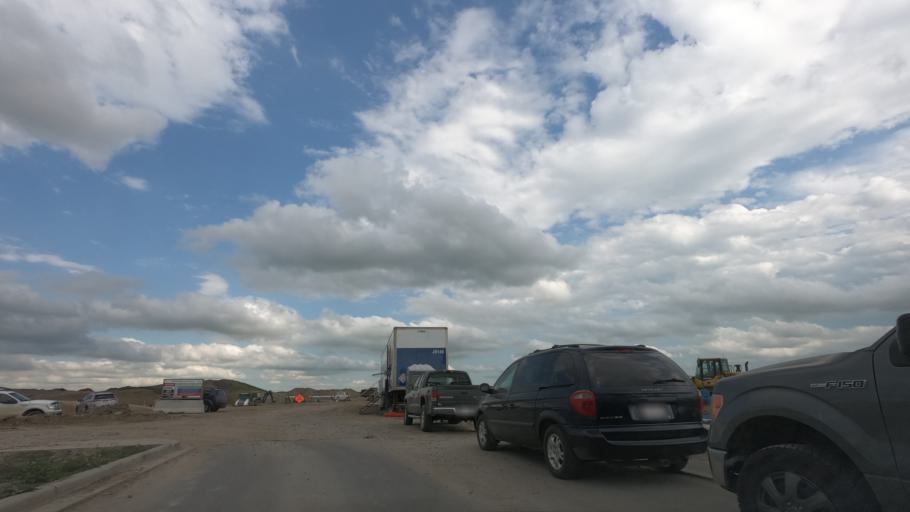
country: CA
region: Alberta
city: Airdrie
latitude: 51.2590
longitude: -113.9799
